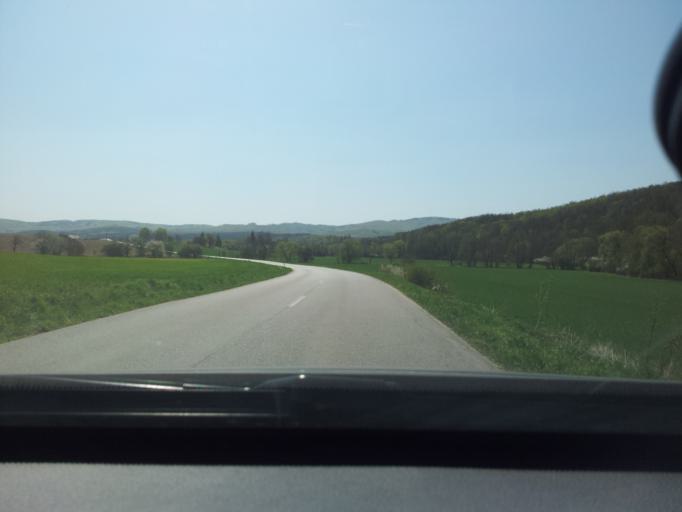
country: SK
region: Nitriansky
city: Partizanske
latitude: 48.5569
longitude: 18.3299
